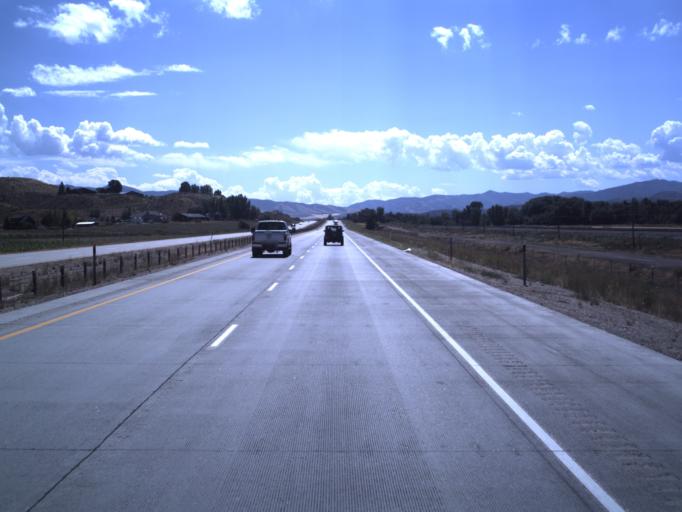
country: US
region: Utah
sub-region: Morgan County
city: Mountain Green
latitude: 41.0939
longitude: -111.7388
